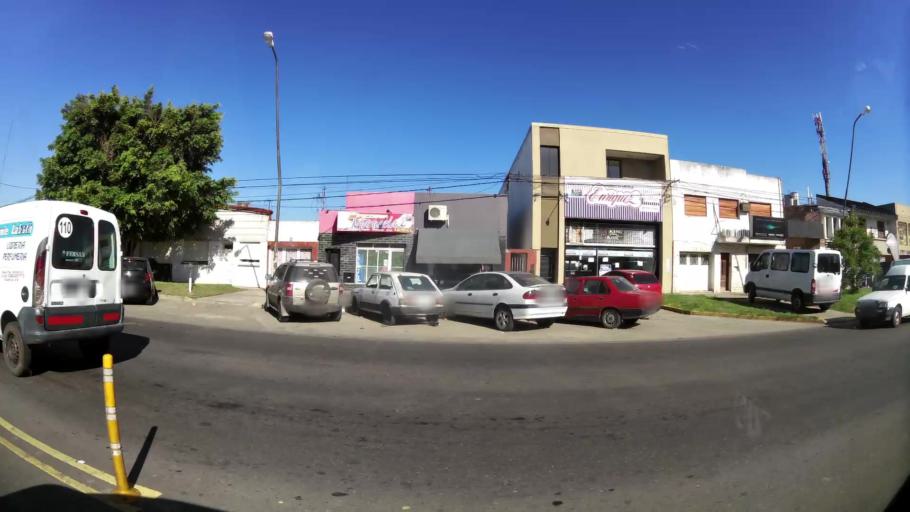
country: AR
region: Santa Fe
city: Santa Fe de la Vera Cruz
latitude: -31.6150
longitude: -60.6968
